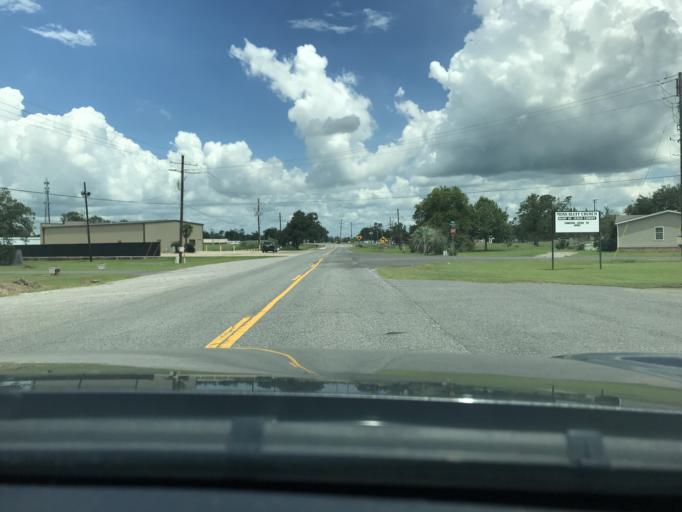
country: US
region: Louisiana
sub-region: Calcasieu Parish
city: Moss Bluff
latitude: 30.3075
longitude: -93.1933
